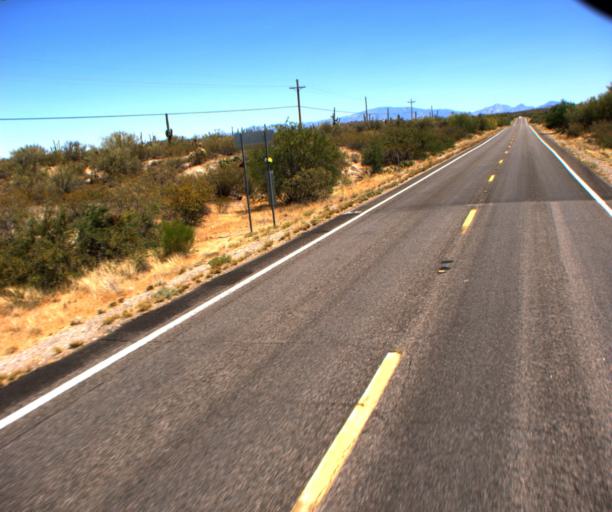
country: US
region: Arizona
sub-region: Pima County
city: Catalina
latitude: 32.7132
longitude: -111.1020
